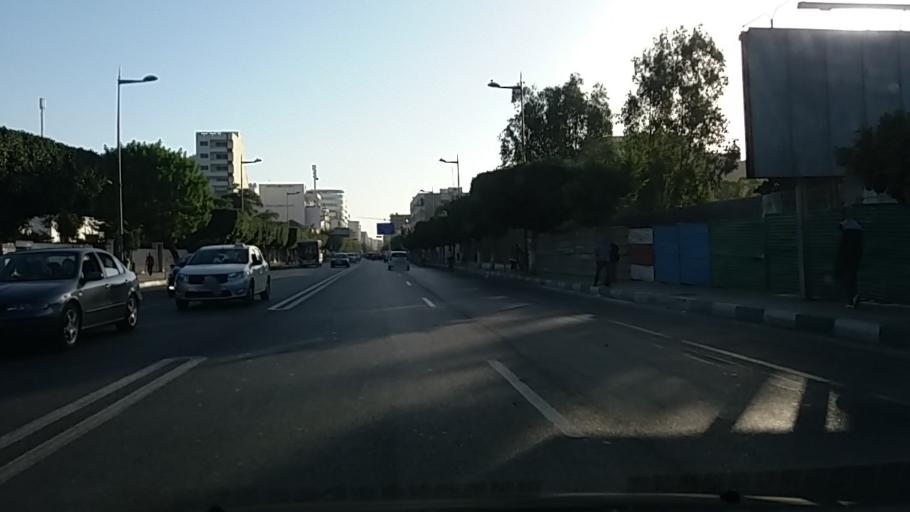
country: MA
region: Gharb-Chrarda-Beni Hssen
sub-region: Kenitra Province
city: Kenitra
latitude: 34.2627
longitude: -6.5769
